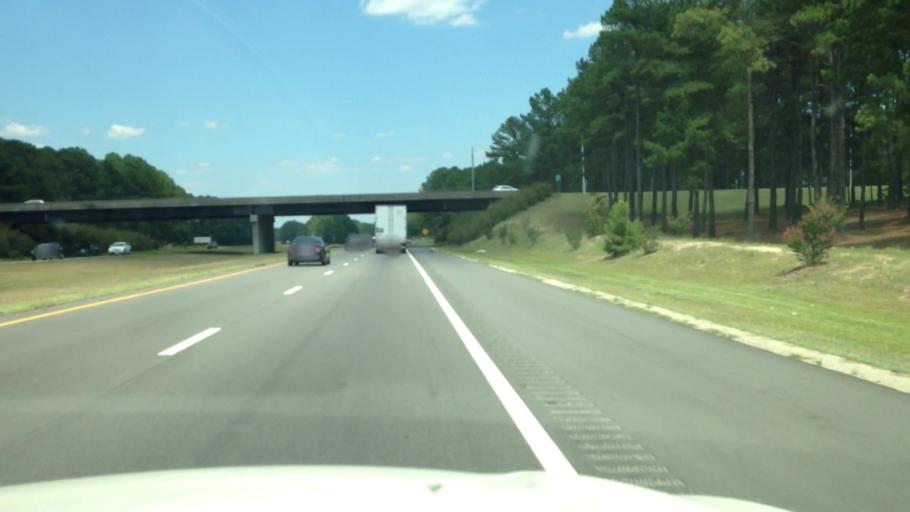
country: US
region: North Carolina
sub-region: Cumberland County
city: Hope Mills
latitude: 34.9376
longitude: -78.9237
